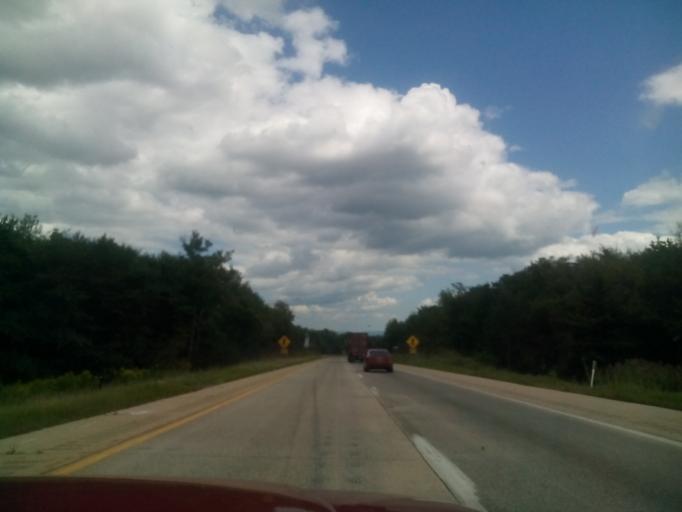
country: US
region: Pennsylvania
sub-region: Monroe County
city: Emerald Lakes
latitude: 41.0691
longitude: -75.3972
